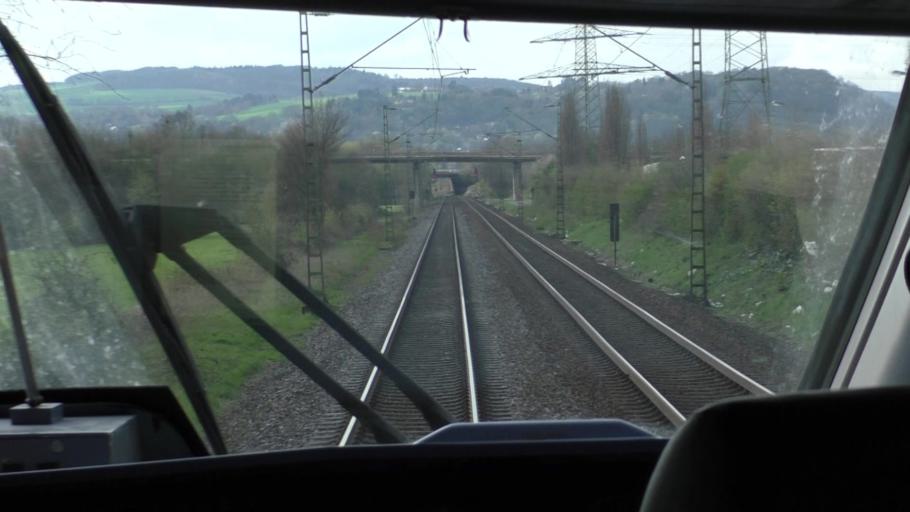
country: DE
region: Rheinland-Pfalz
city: Andernach
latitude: 50.4289
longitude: 7.4275
